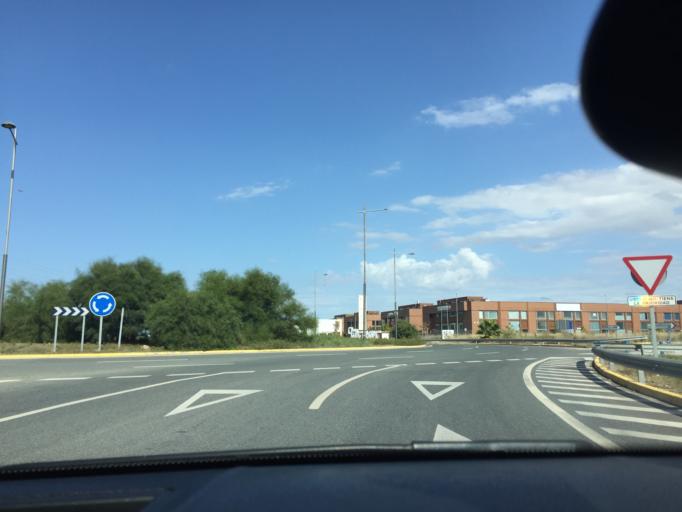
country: ES
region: Andalusia
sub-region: Provincia de Sevilla
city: Gelves
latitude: 37.3219
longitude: -6.0316
